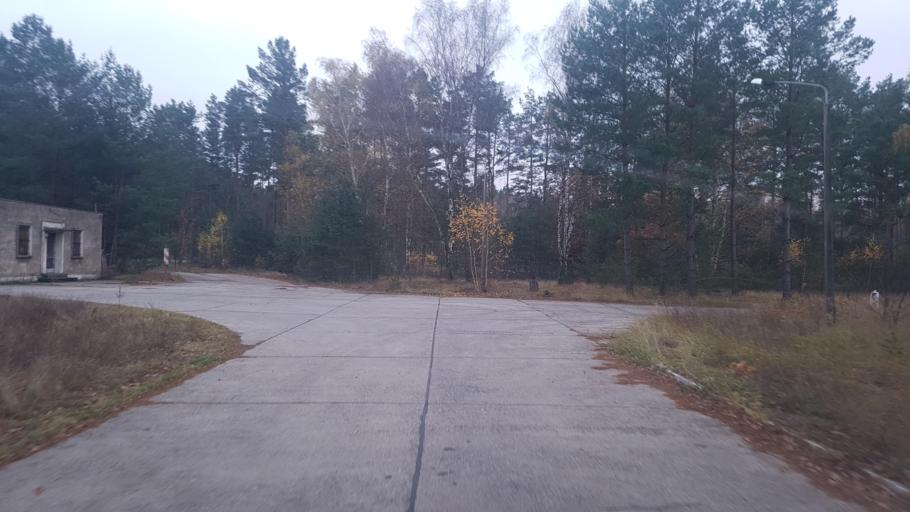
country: DE
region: Brandenburg
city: Gross Kreutz
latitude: 52.3558
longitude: 12.7757
